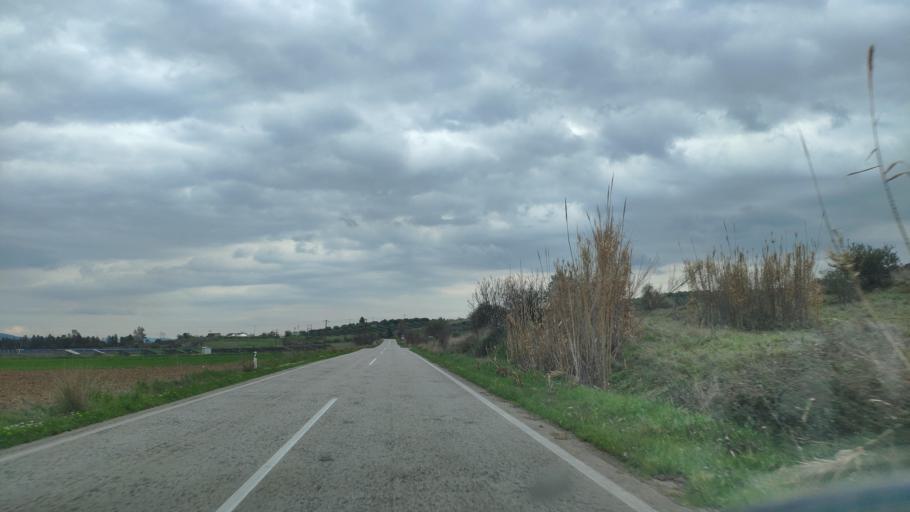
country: GR
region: Central Greece
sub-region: Nomos Voiotias
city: Livadeia
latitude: 38.4824
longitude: 22.9060
